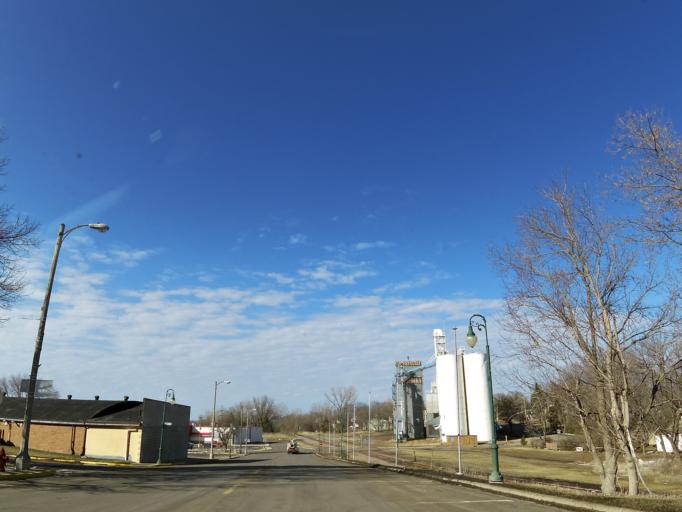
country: US
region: Minnesota
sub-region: Le Sueur County
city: Montgomery
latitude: 44.4407
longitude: -93.5812
